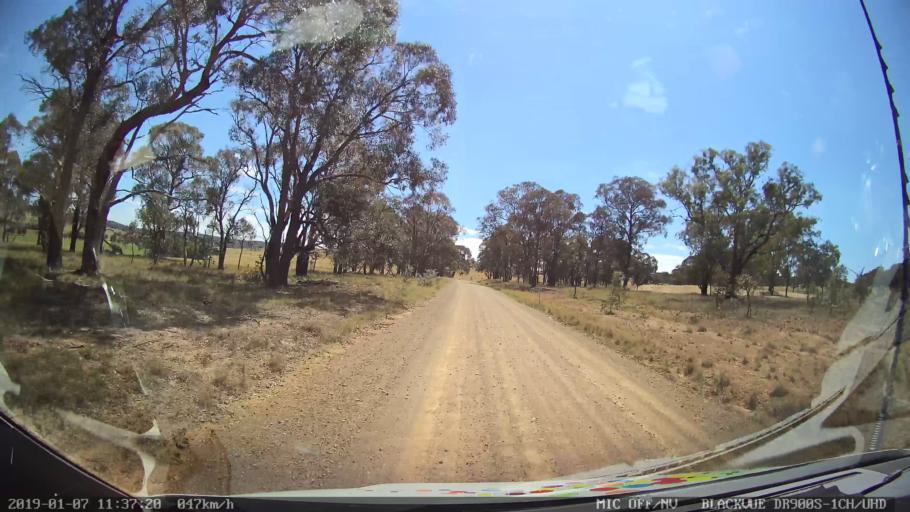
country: AU
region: New South Wales
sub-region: Armidale Dumaresq
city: Armidale
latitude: -30.3714
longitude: 151.5648
